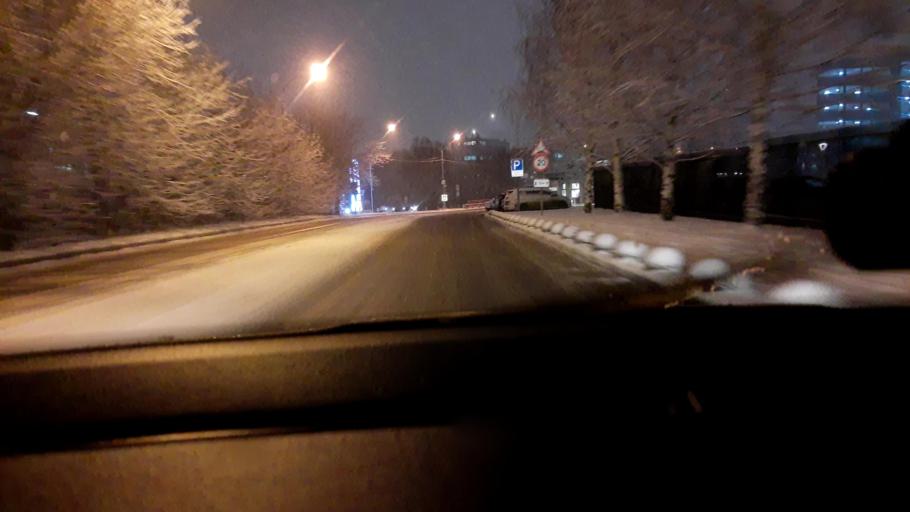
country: RU
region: Moskovskaya
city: Zarech'ye
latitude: 55.6956
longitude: 37.3982
